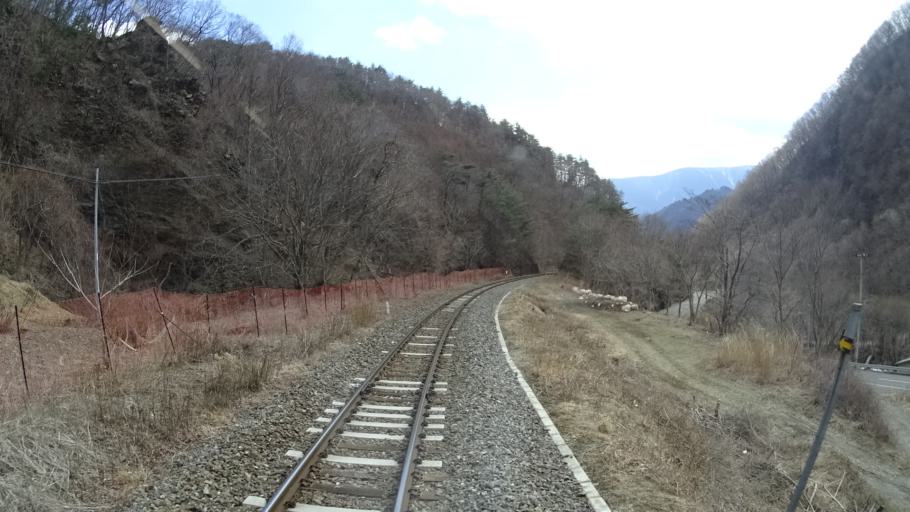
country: JP
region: Iwate
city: Kamaishi
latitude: 39.2748
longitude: 141.7245
